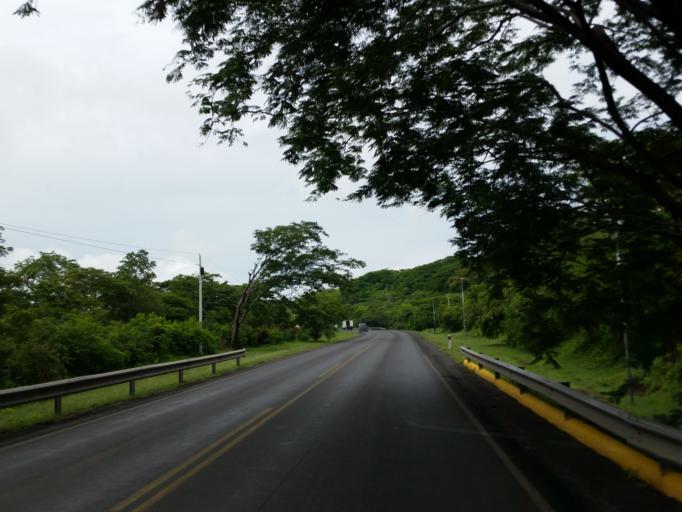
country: NI
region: Leon
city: Nagarote
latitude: 12.2788
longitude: -86.5265
